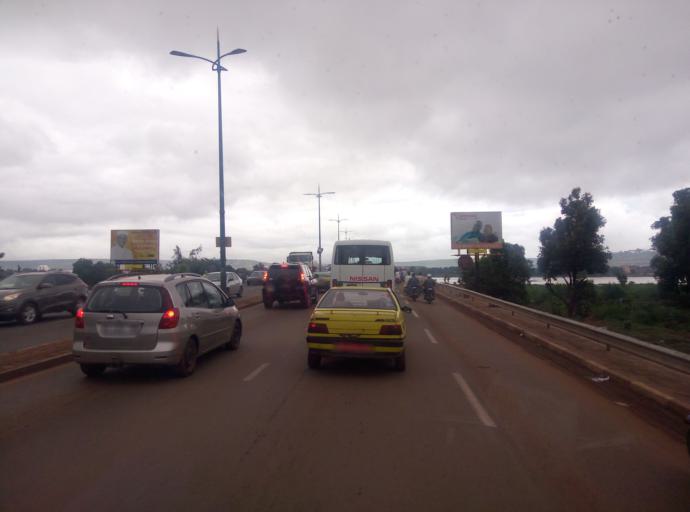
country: ML
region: Bamako
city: Bamako
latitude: 12.6189
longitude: -8.0013
